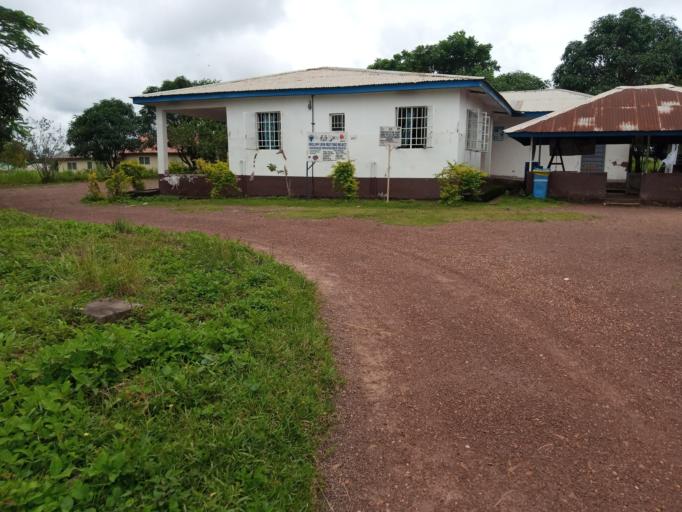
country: SL
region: Southern Province
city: Largo
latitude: 8.1934
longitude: -12.0616
